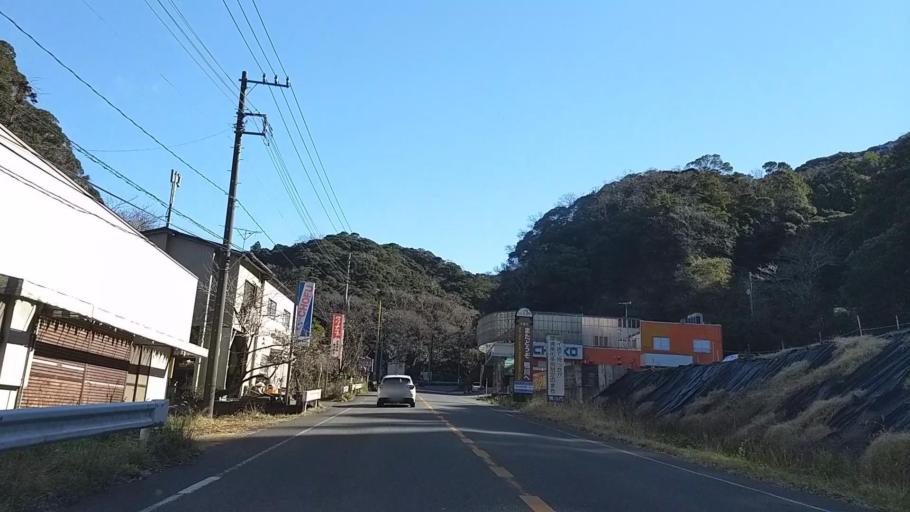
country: JP
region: Chiba
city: Kawaguchi
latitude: 35.1198
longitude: 140.2040
